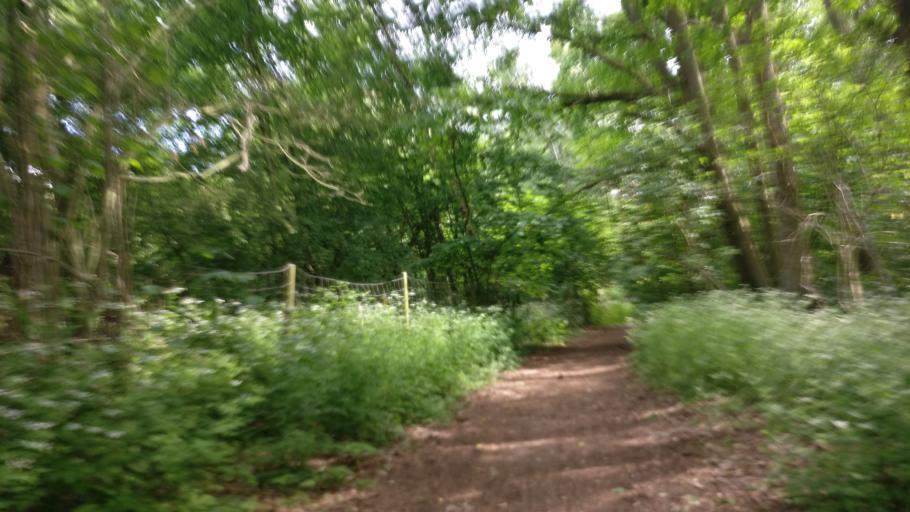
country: DE
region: North Rhine-Westphalia
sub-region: Regierungsbezirk Detmold
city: Lage
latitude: 52.0132
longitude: 8.7616
